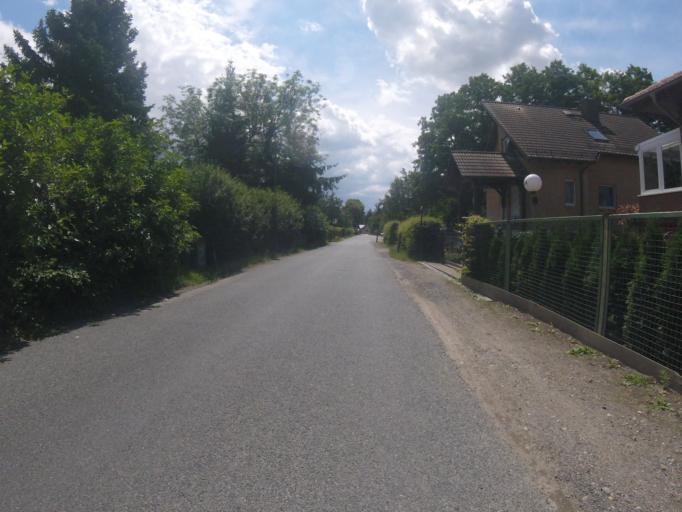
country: DE
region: Brandenburg
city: Bestensee
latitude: 52.2713
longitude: 13.6414
